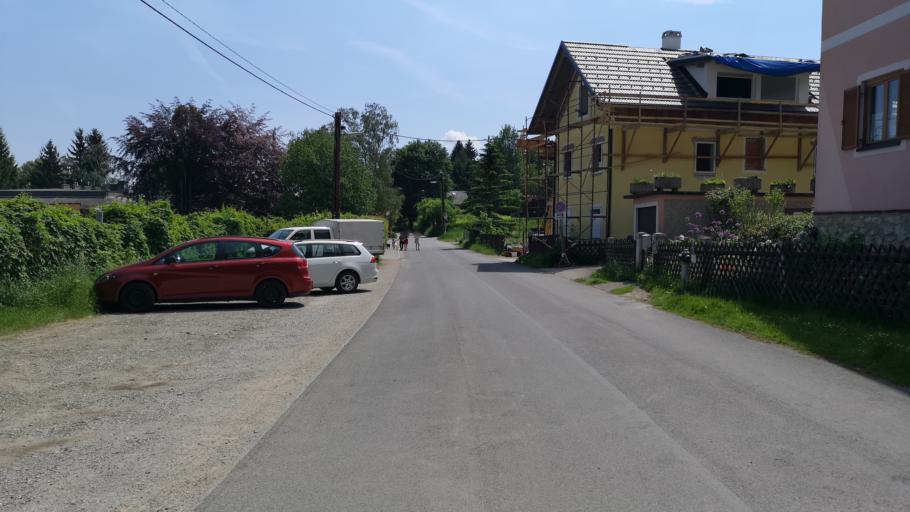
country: AT
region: Styria
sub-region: Politischer Bezirk Graz-Umgebung
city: Seiersberg
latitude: 47.0241
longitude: 15.3961
